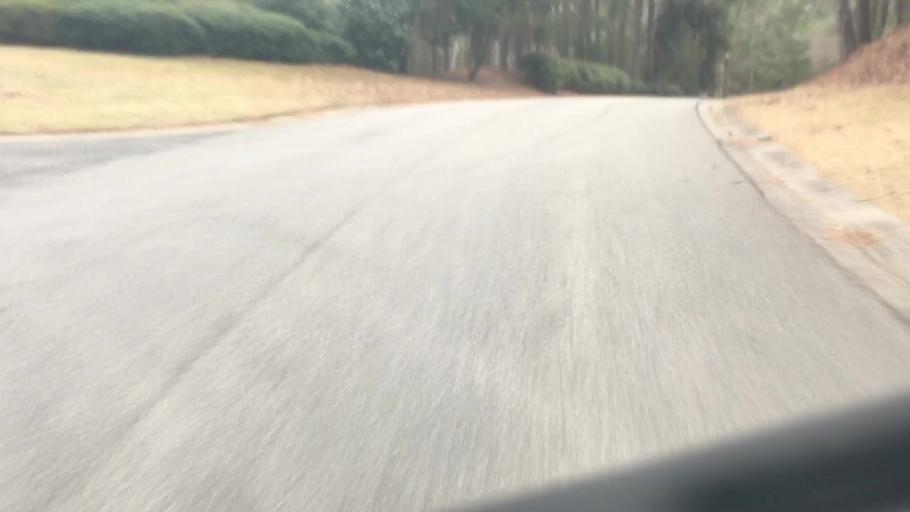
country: US
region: Alabama
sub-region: Shelby County
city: Helena
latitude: 33.3466
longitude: -86.8199
